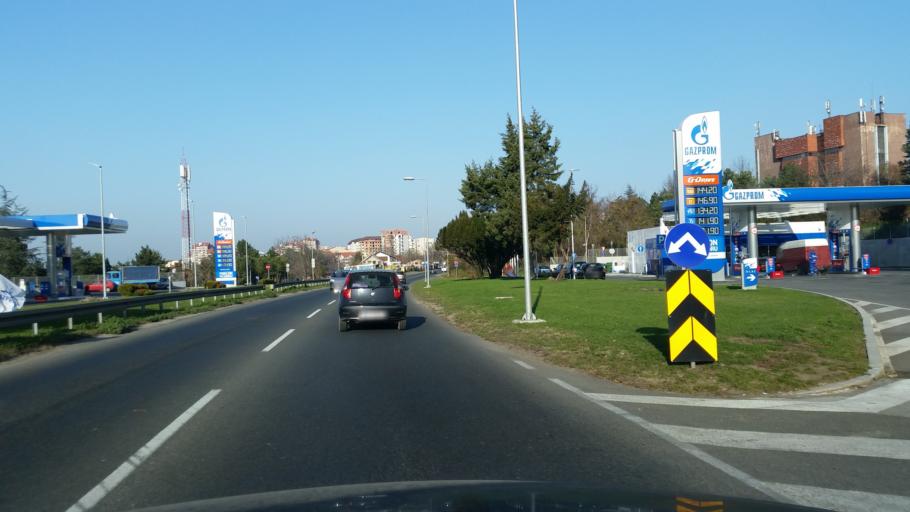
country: RS
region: Central Serbia
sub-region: Belgrade
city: Rakovica
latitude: 44.7511
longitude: 20.4125
